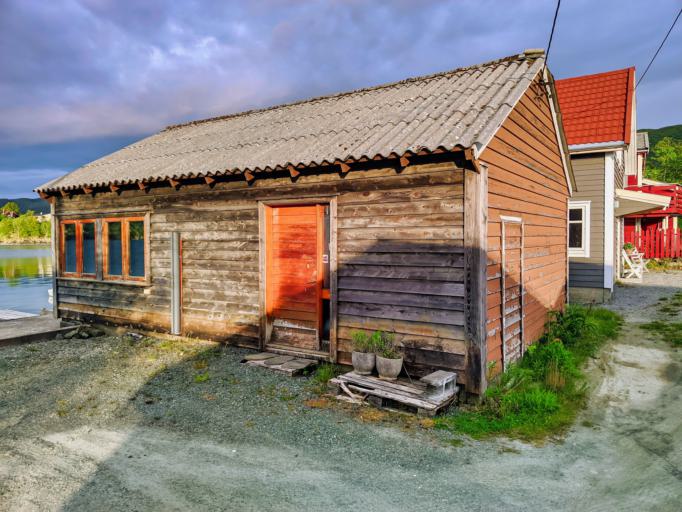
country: NO
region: Hordaland
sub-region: Tysnes
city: Uggdal
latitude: 60.0448
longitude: 5.5279
